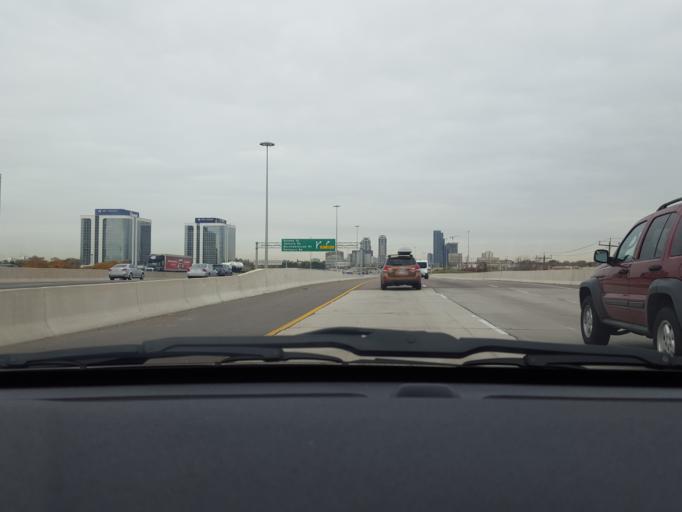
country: CA
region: Ontario
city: Etobicoke
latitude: 43.6228
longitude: -79.5540
